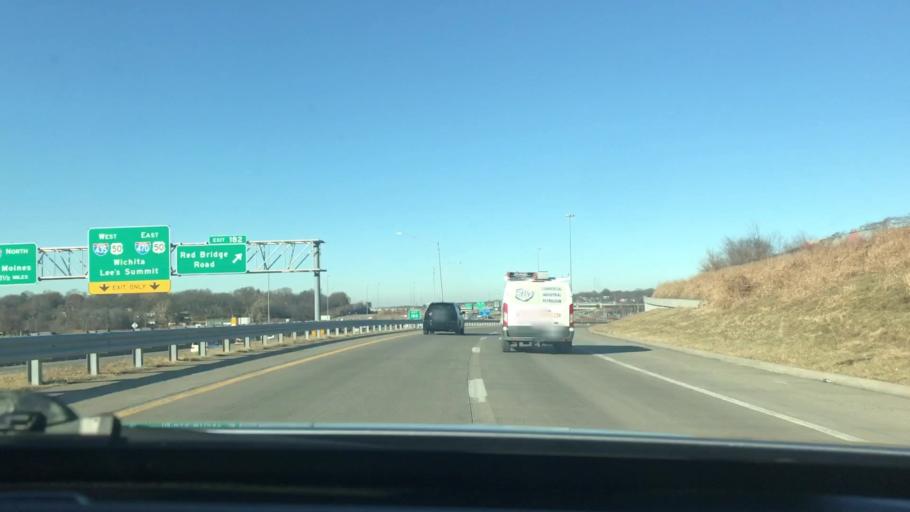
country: US
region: Missouri
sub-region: Jackson County
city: Grandview
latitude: 38.9196
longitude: -94.5273
